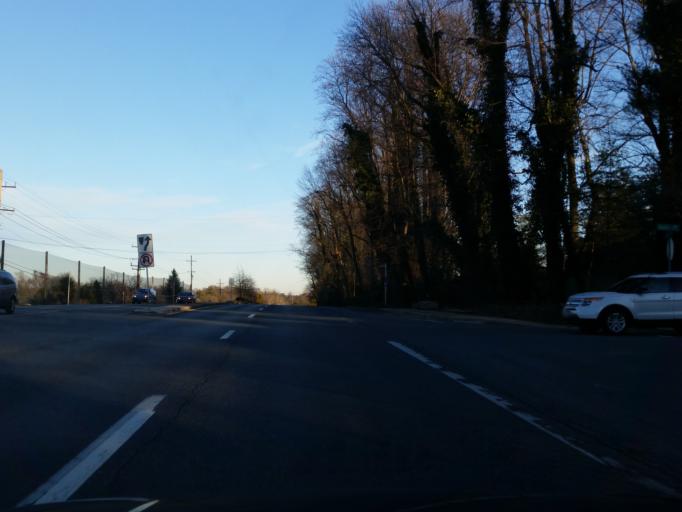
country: US
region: Maryland
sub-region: Montgomery County
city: Bethesda
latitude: 38.9705
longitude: -77.1164
